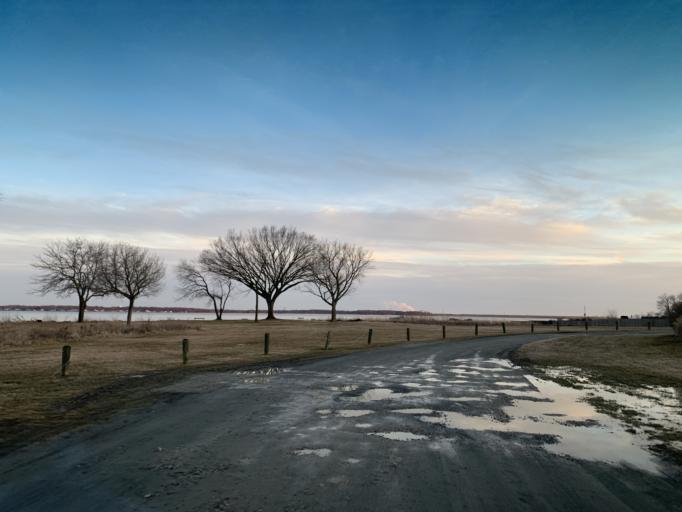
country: US
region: Delaware
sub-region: New Castle County
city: New Castle
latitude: 39.6616
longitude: -75.5595
